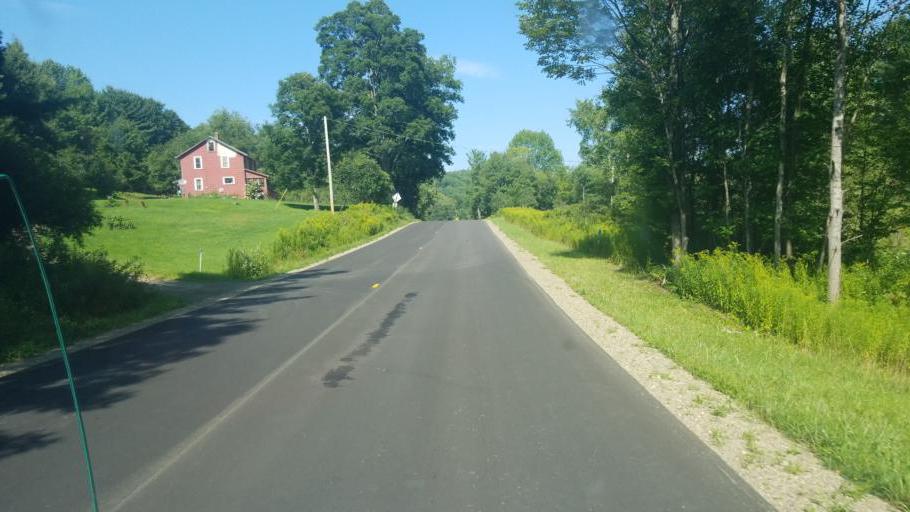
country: US
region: New York
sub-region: Allegany County
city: Wellsville
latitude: 42.0634
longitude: -78.0388
